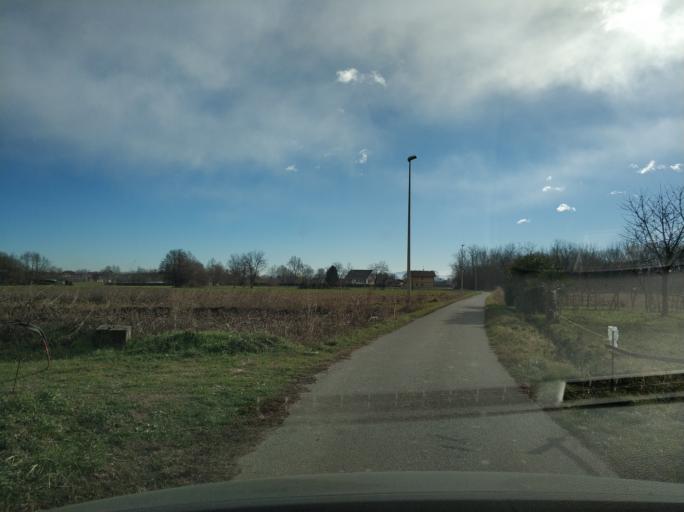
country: IT
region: Piedmont
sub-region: Provincia di Torino
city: Robassomero
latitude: 45.2172
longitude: 7.5778
